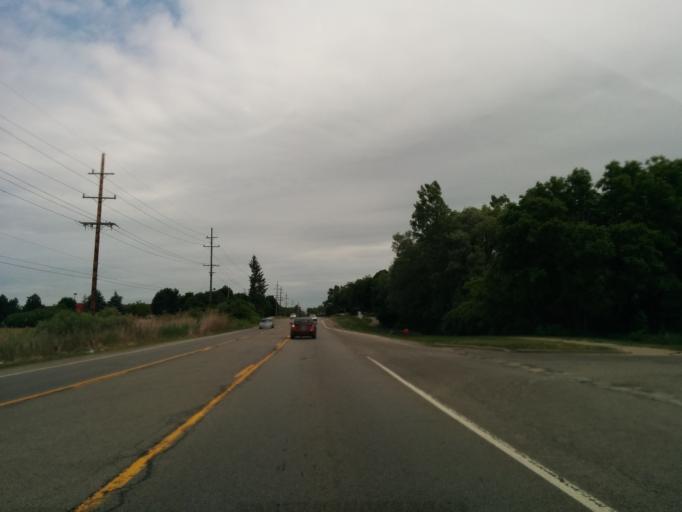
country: US
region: Michigan
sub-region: Oakland County
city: Walled Lake
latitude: 42.5297
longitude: -83.4377
